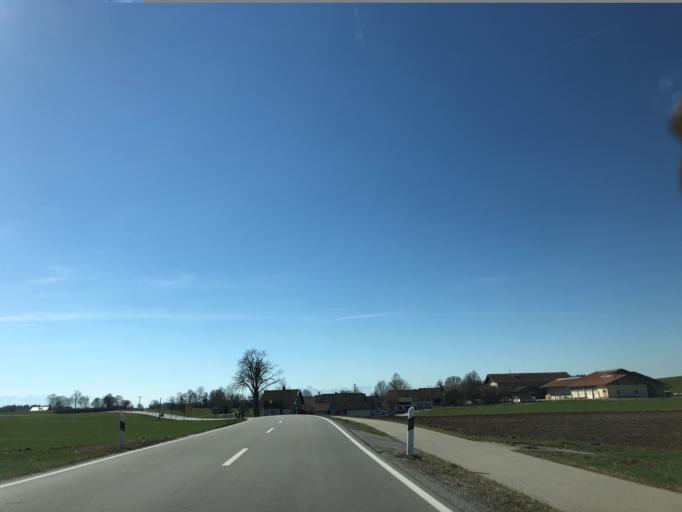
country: DE
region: Bavaria
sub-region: Upper Bavaria
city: Pfaffing
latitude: 48.0661
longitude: 12.1104
